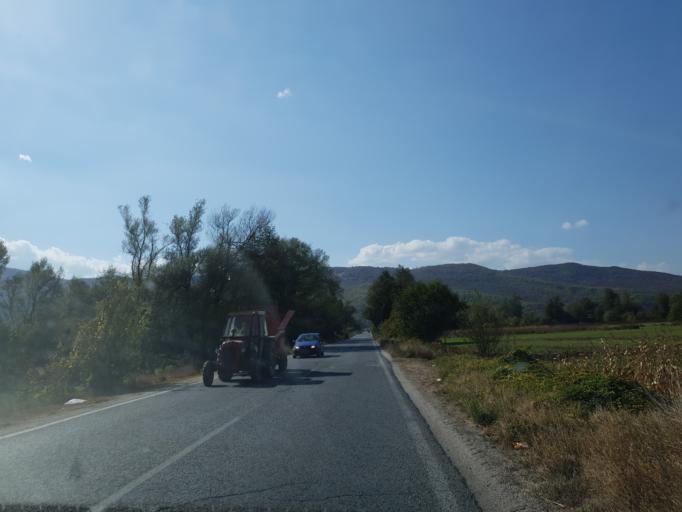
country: MK
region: Kicevo
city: Kicevo
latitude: 41.4808
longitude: 20.9917
